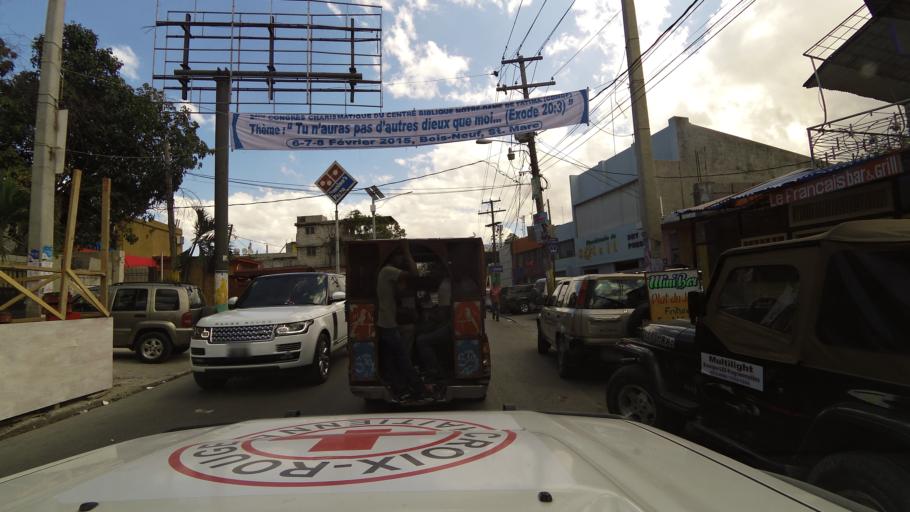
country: HT
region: Ouest
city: Petionville
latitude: 18.5184
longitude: -72.2913
